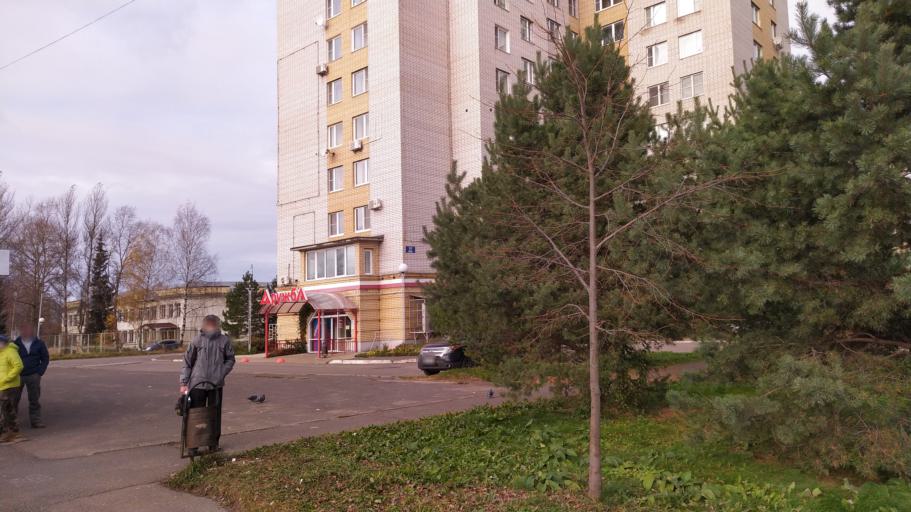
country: RU
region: Jaroslavl
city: Rybinsk
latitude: 58.0561
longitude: 38.8043
